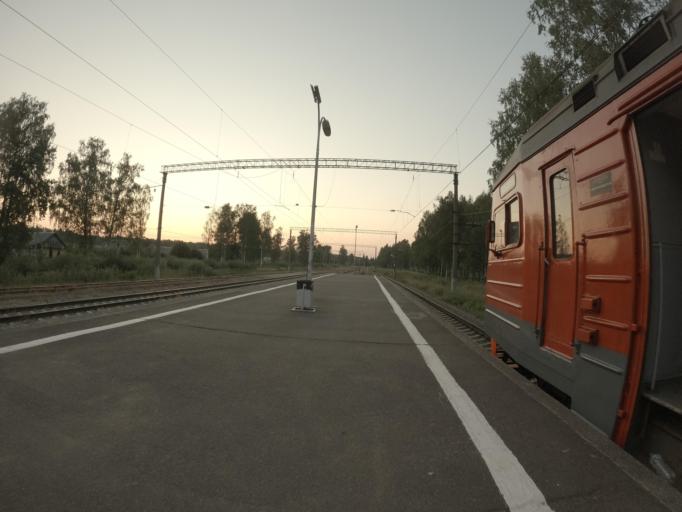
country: RU
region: Leningrad
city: Pavlovo
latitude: 59.8446
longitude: 30.9286
